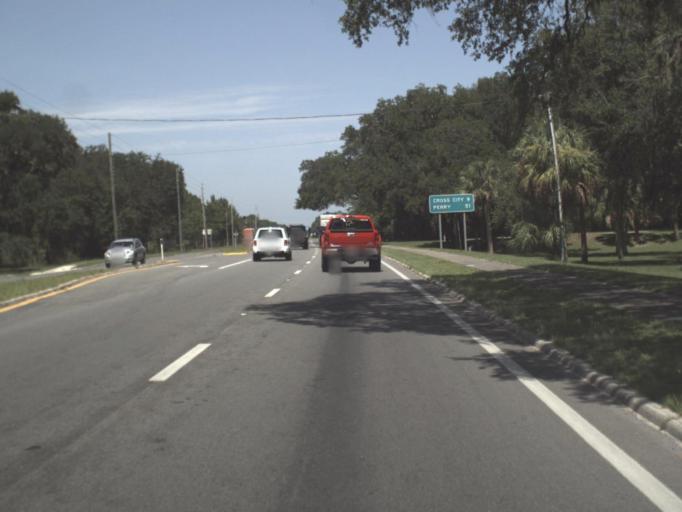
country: US
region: Florida
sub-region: Levy County
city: Manatee Road
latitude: 29.6019
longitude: -82.9841
